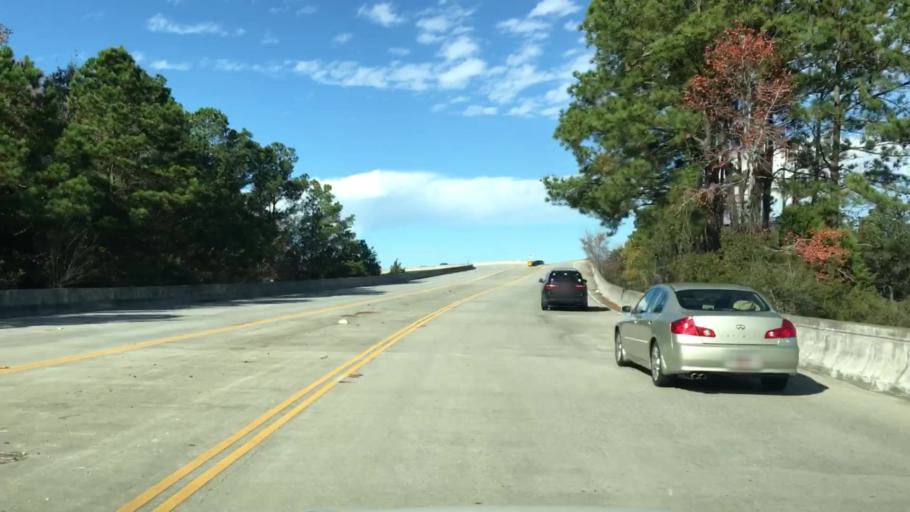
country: US
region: South Carolina
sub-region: Charleston County
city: Charleston
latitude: 32.7780
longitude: -79.9677
